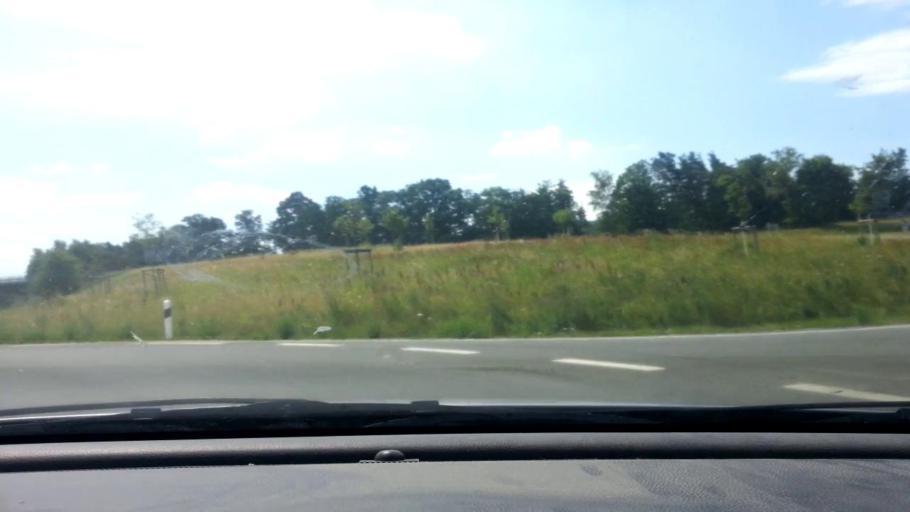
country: DE
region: Bavaria
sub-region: Upper Franconia
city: Neunkirchen am Main
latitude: 49.9271
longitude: 11.6306
